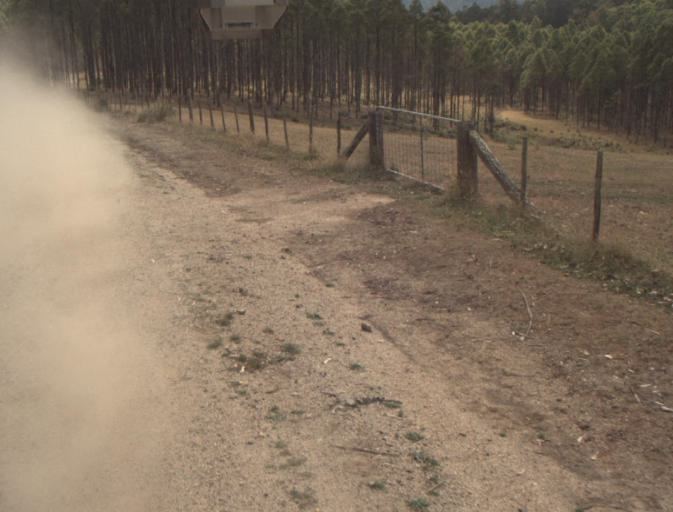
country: AU
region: Tasmania
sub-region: Dorset
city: Scottsdale
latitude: -41.4134
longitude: 147.5258
